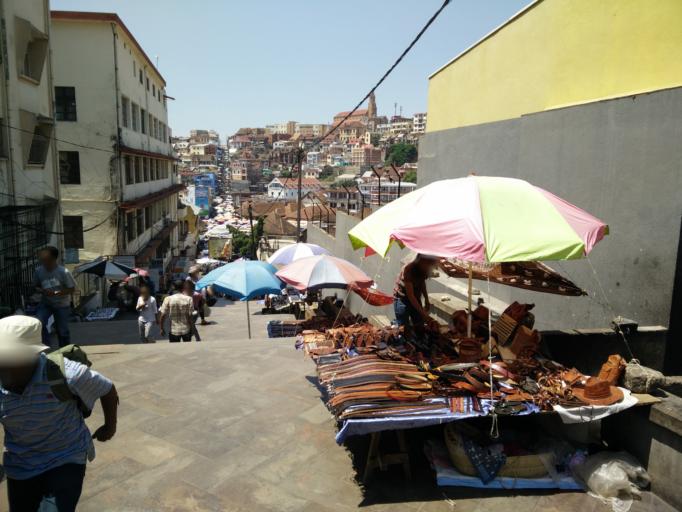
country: MG
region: Analamanga
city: Antananarivo
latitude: -18.9092
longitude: 47.5256
